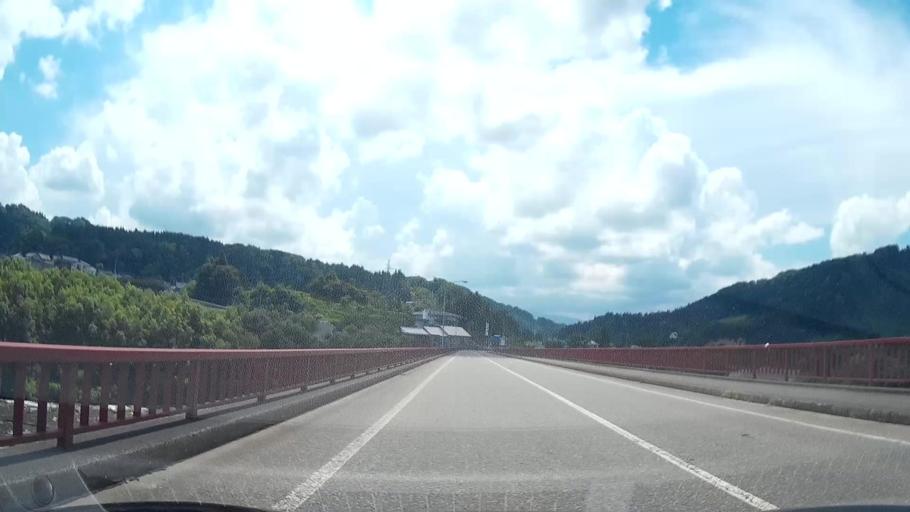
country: JP
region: Niigata
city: Tokamachi
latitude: 37.0115
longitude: 138.6482
